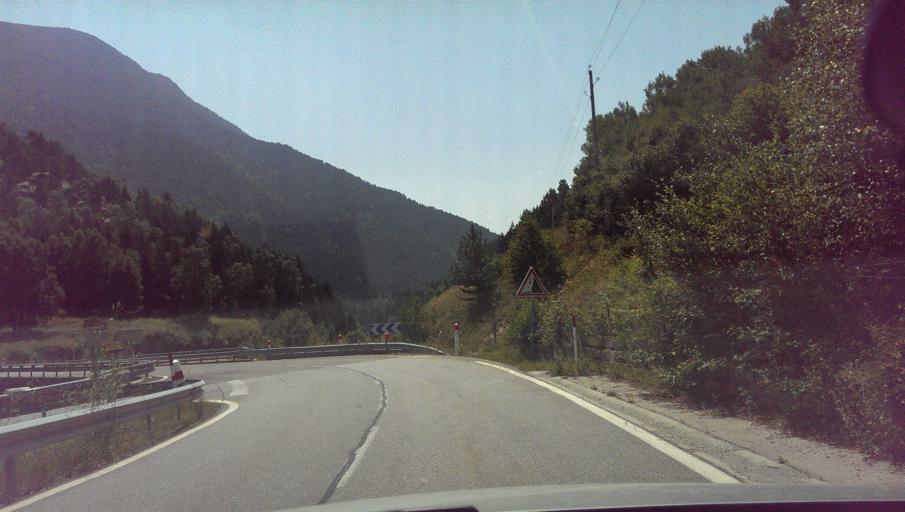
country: AD
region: Encamp
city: Pas de la Casa
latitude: 42.5462
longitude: 1.8253
